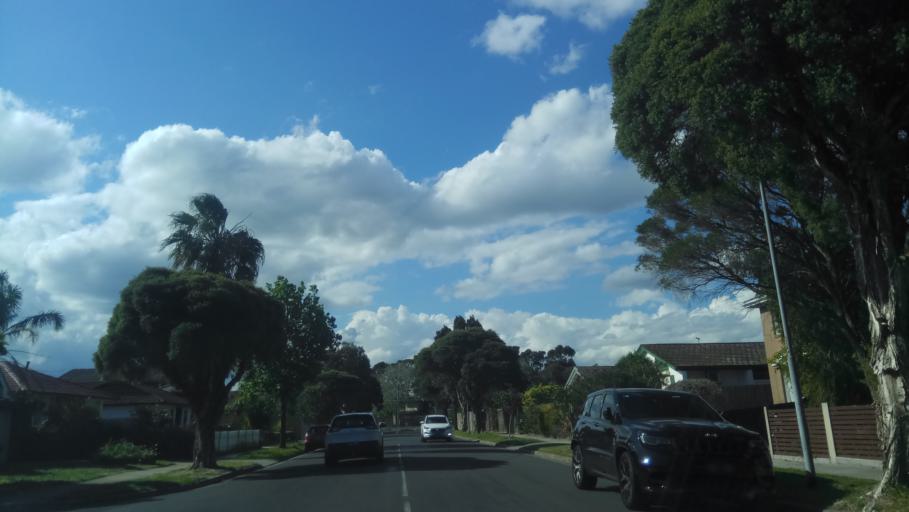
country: AU
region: Victoria
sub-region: Kingston
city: Dingley Village
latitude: -37.9866
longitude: 145.1352
